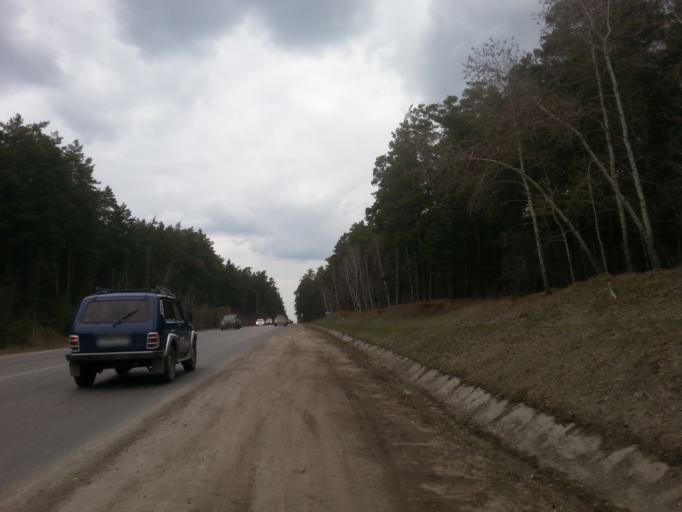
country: RU
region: Altai Krai
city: Yuzhnyy
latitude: 53.2695
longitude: 83.7256
